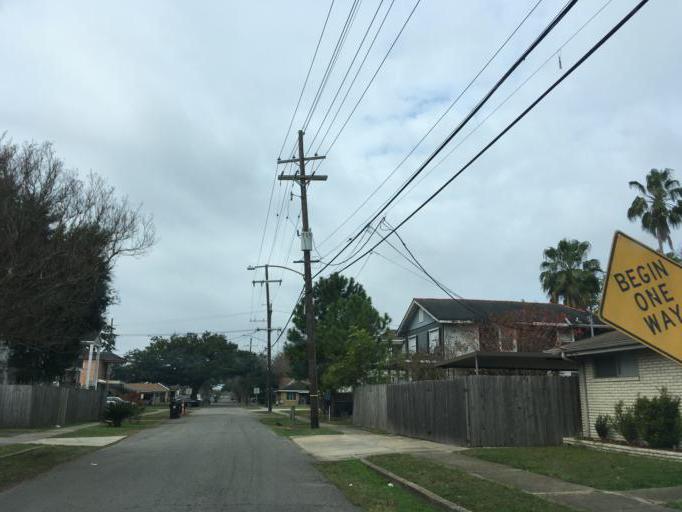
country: US
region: Louisiana
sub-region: Orleans Parish
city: New Orleans
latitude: 29.9898
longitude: -90.0599
